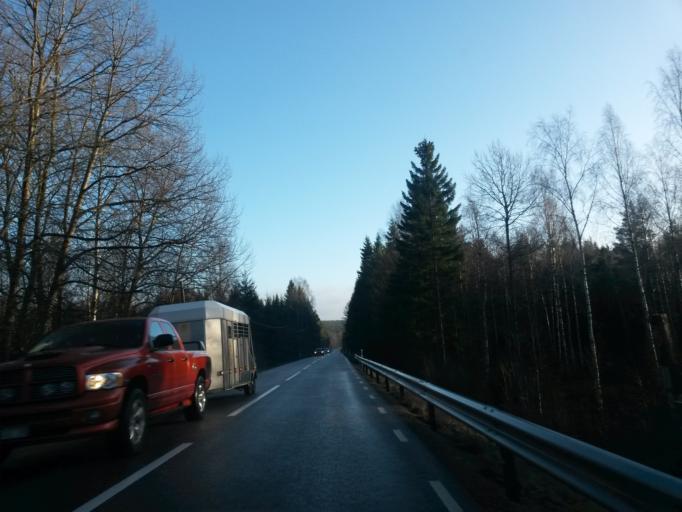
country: SE
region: Vaestra Goetaland
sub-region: Vargarda Kommun
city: Vargarda
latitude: 57.9165
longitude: 12.8849
